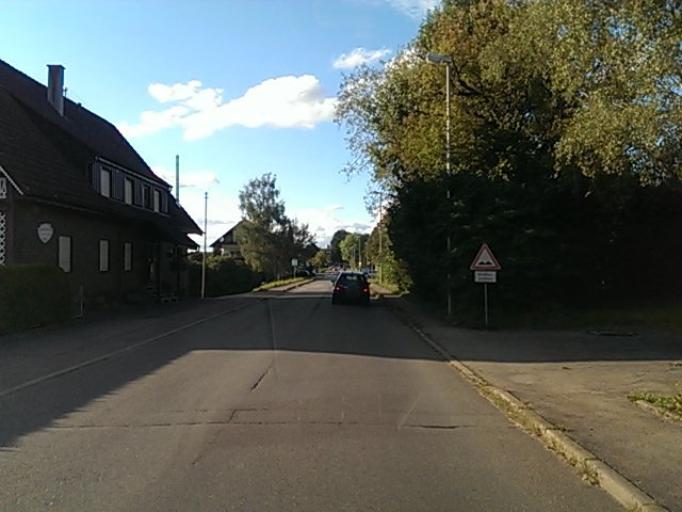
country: DE
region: Baden-Wuerttemberg
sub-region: Freiburg Region
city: Dornhan
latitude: 48.3245
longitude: 8.4668
